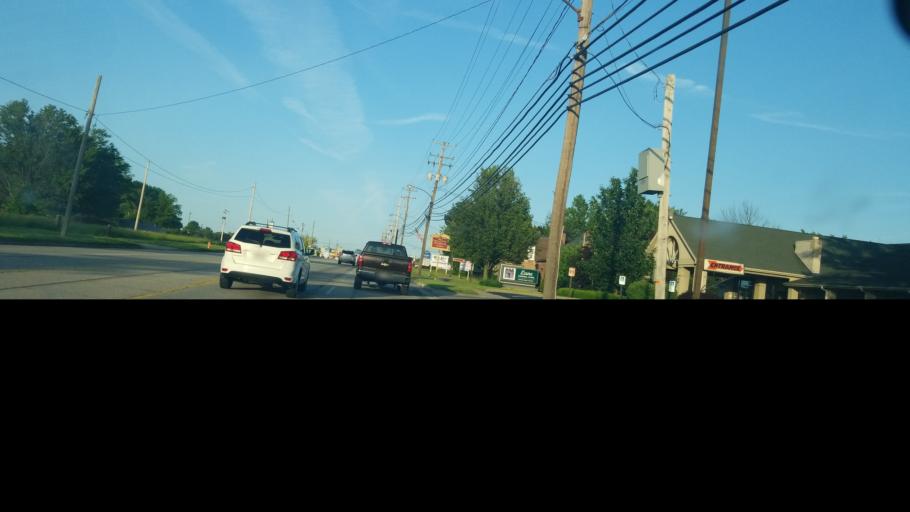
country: US
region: Ohio
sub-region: Mahoning County
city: Austintown
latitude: 41.0995
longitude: -80.7707
